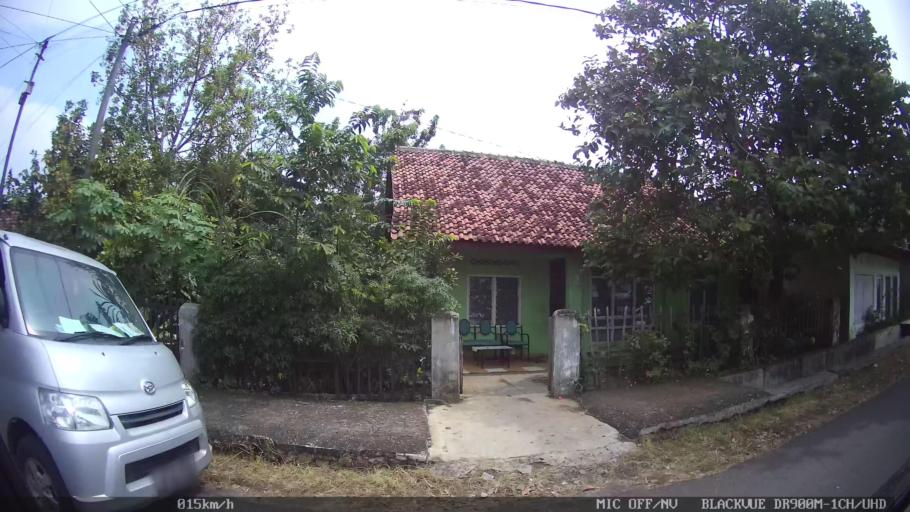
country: ID
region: Lampung
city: Bandarlampung
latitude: -5.4191
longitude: 105.2665
